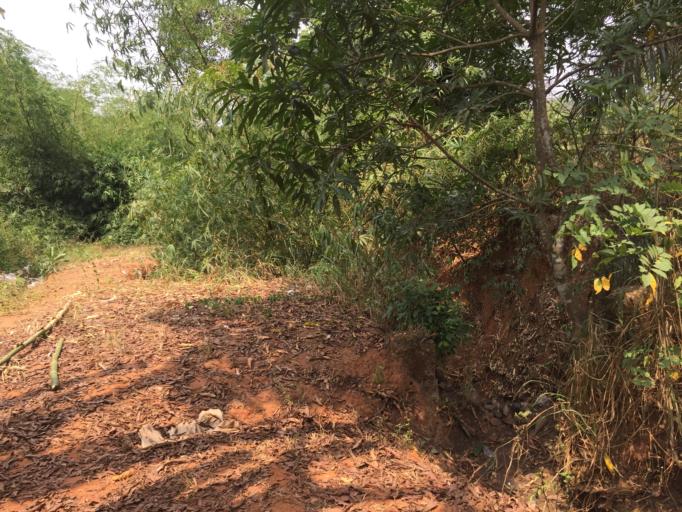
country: NG
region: Imo
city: Ihuo
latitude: 5.5131
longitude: 7.1061
